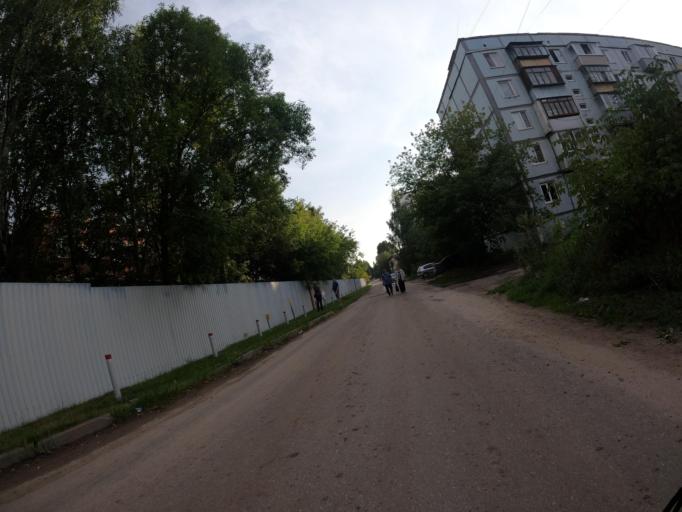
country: RU
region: Moskovskaya
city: Il'inskiy
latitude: 55.6341
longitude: 38.1057
